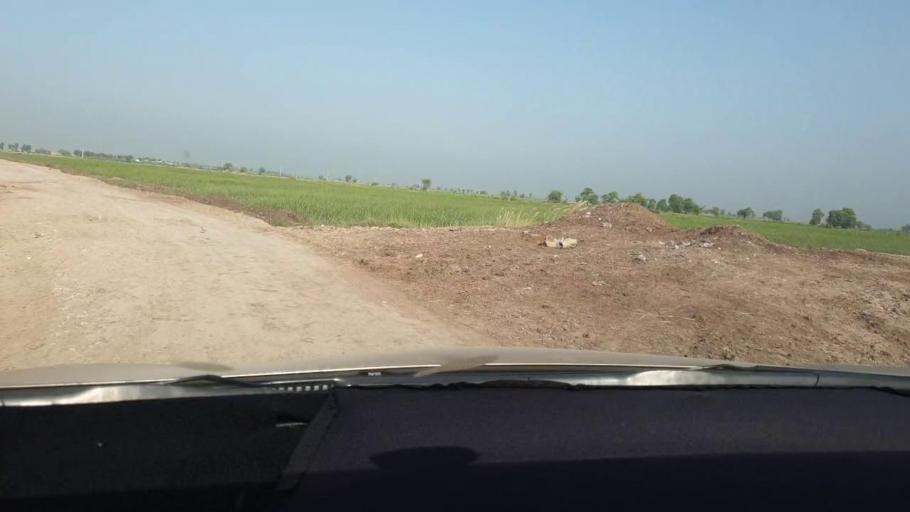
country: PK
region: Sindh
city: Miro Khan
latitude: 27.7566
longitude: 68.1404
